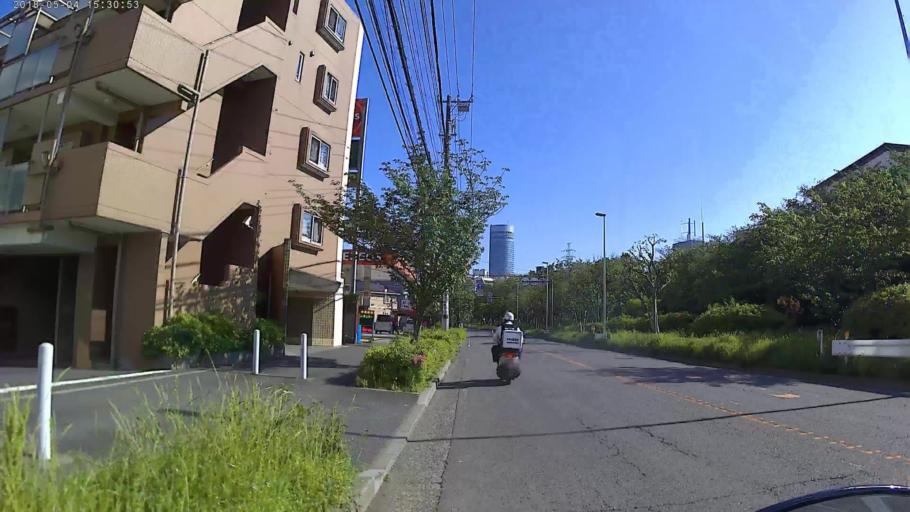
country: JP
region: Kanagawa
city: Yokohama
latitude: 35.5177
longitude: 139.6208
